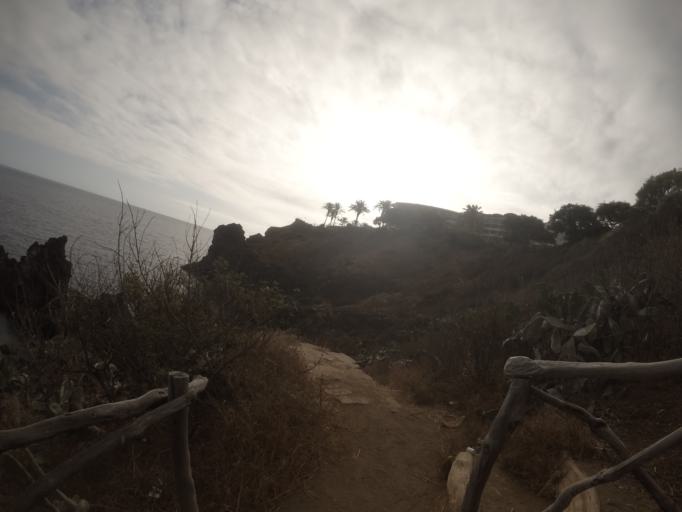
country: PT
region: Madeira
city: Camara de Lobos
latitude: 32.6336
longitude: -16.9437
